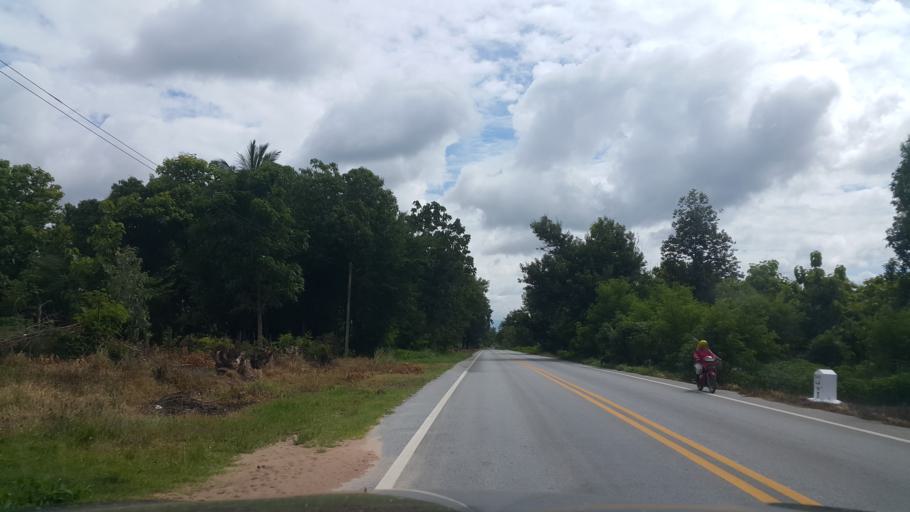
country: TH
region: Uttaradit
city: Thong Saen Khan
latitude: 17.3877
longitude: 100.2905
